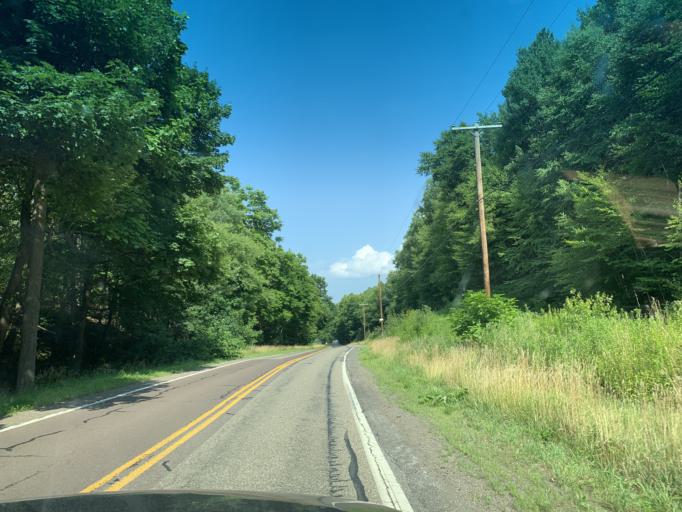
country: US
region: Pennsylvania
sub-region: Schuylkill County
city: Ashland
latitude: 40.8045
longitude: -76.3357
